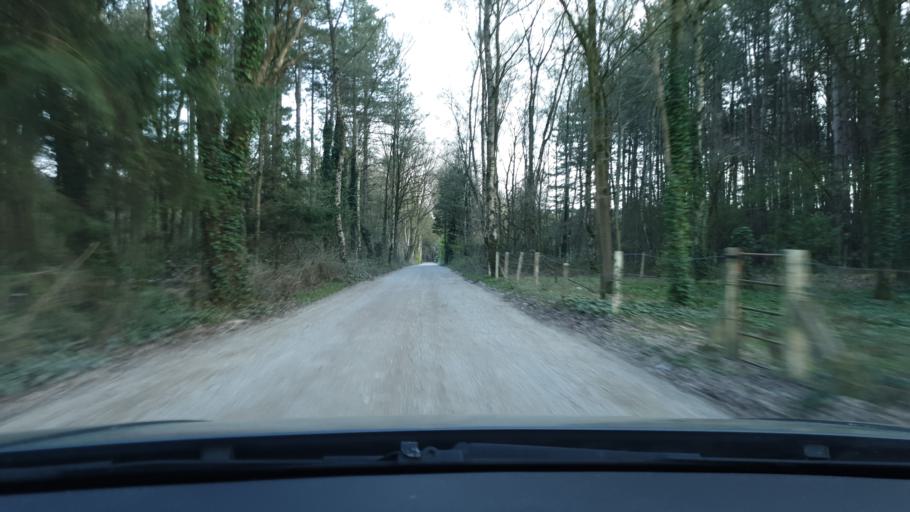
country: BE
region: Flanders
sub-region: Provincie Antwerpen
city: Geel
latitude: 51.1354
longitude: 4.9997
